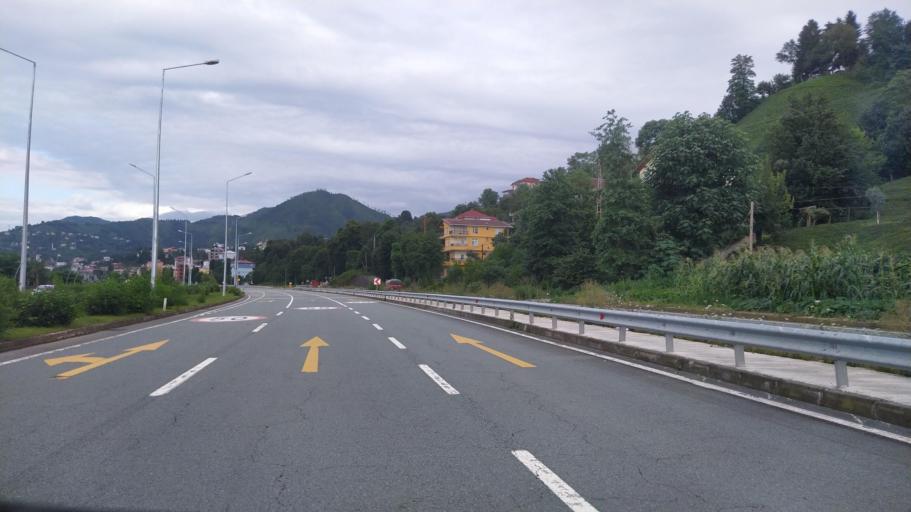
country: TR
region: Rize
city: Ardesen
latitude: 41.2099
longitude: 41.0385
